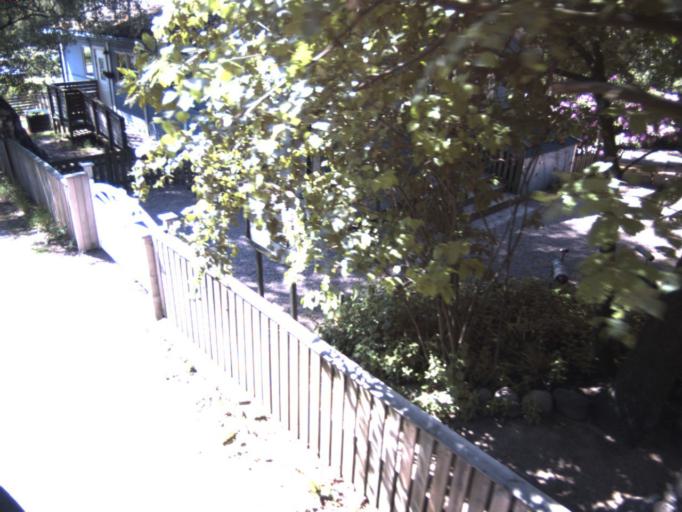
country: SE
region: Skane
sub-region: Helsingborg
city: Rydeback
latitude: 56.0132
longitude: 12.7444
